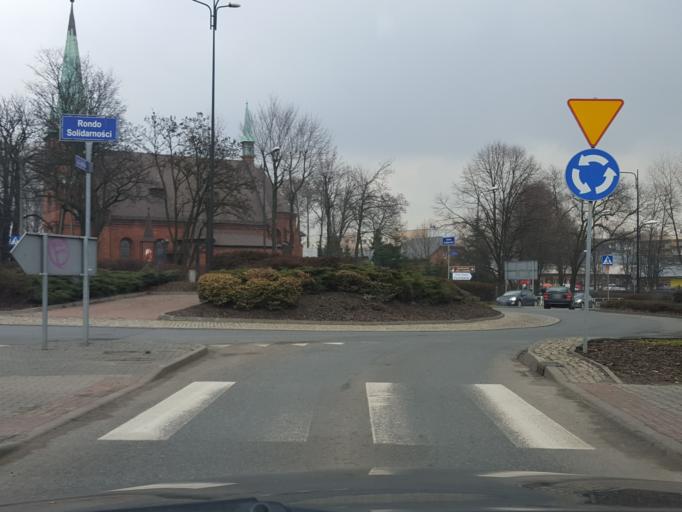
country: PL
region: Silesian Voivodeship
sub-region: Ruda Slaska
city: Ruda Slaska
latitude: 50.2431
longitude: 18.8411
